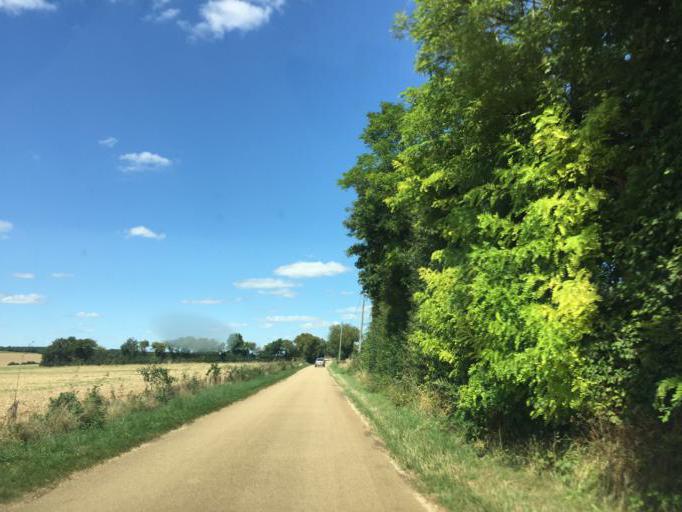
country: FR
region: Bourgogne
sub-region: Departement de l'Yonne
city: Fontenailles
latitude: 47.5744
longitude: 3.3447
